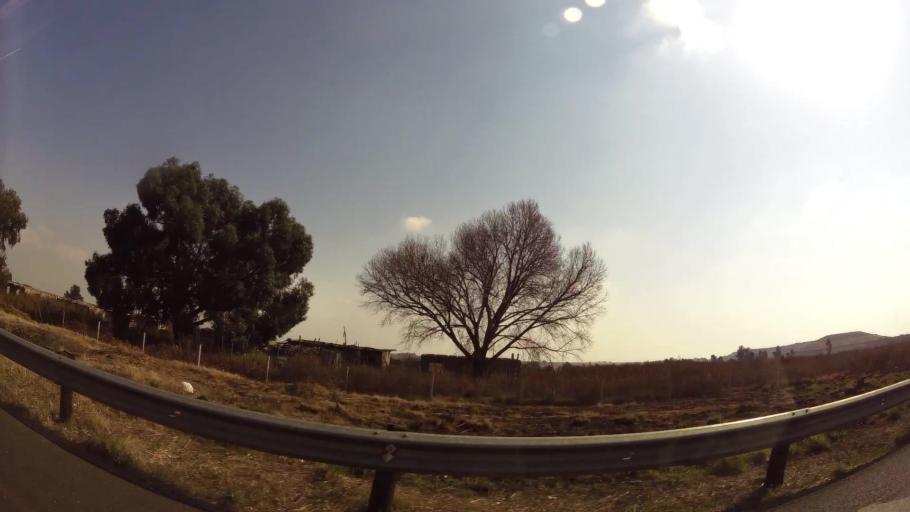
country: ZA
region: Gauteng
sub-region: Ekurhuleni Metropolitan Municipality
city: Springs
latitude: -26.1590
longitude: 28.5201
